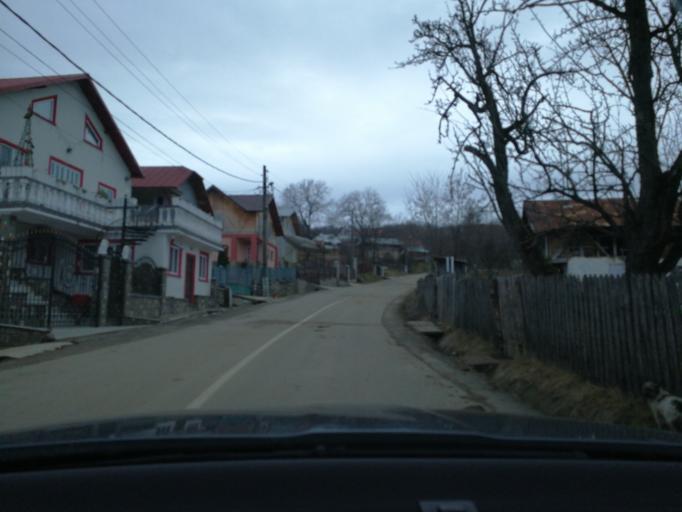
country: RO
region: Prahova
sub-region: Comuna Adunati
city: Ocina de Sus
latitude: 45.1786
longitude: 25.5881
